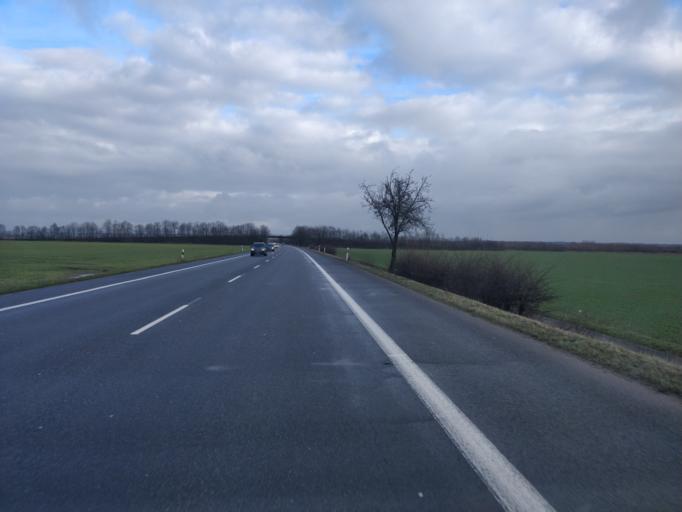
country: DE
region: North Rhine-Westphalia
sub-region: Regierungsbezirk Koln
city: Euskirchen
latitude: 50.6904
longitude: 6.8468
